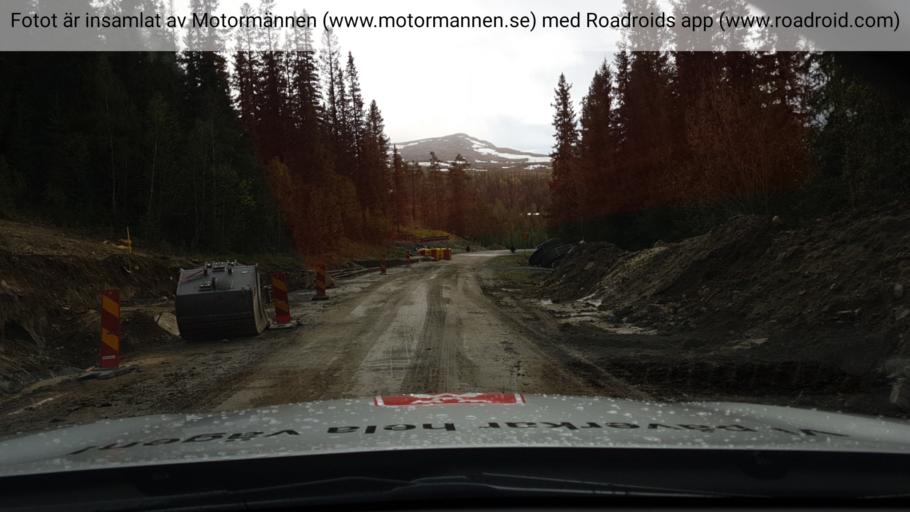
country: SE
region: Jaemtland
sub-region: Are Kommun
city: Jarpen
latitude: 63.0846
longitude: 13.7736
